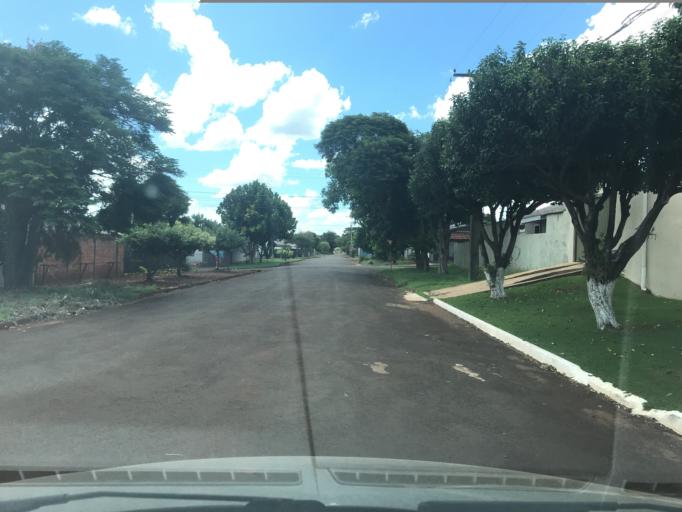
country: BR
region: Parana
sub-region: Palotina
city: Palotina
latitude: -24.2726
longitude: -53.8476
